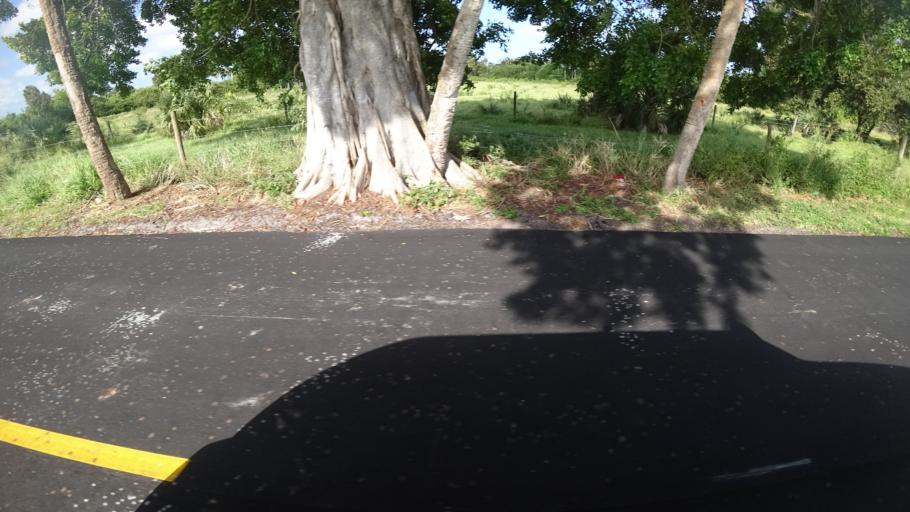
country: US
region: Florida
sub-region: Manatee County
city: Memphis
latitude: 27.5391
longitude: -82.5728
